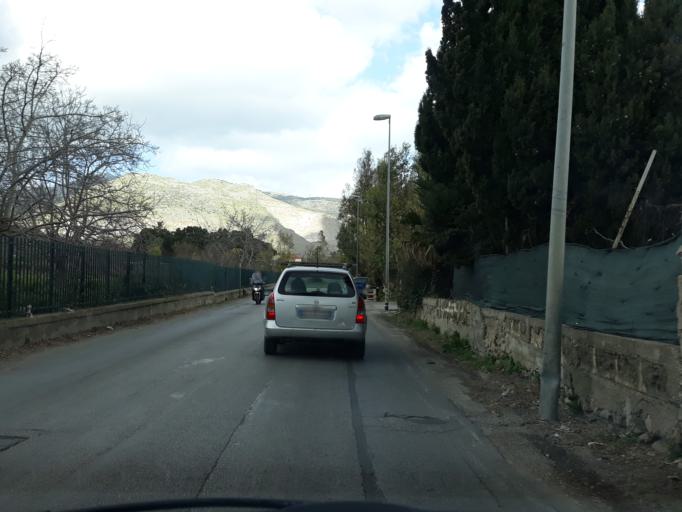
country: IT
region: Sicily
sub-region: Palermo
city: Piano dei Geli
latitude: 38.1147
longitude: 13.3037
